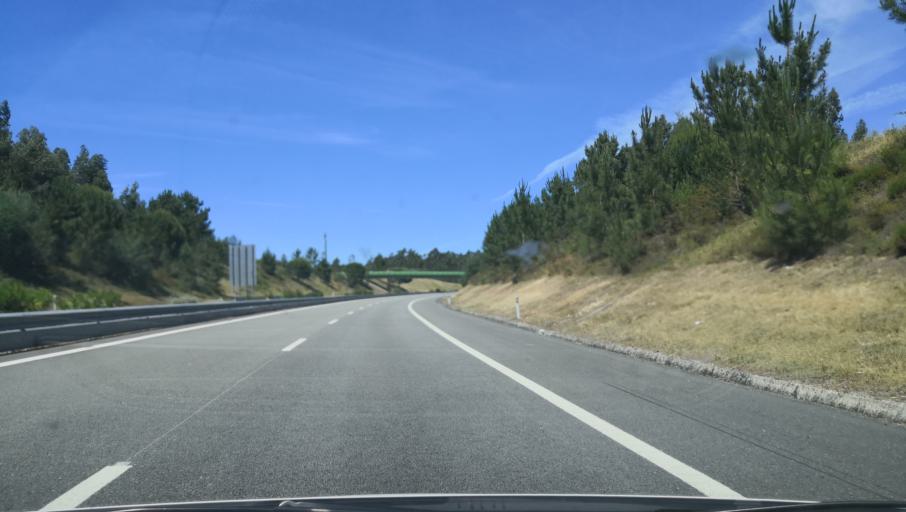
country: PT
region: Coimbra
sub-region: Montemor-O-Velho
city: Montemor-o-Velho
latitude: 40.2202
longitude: -8.6750
